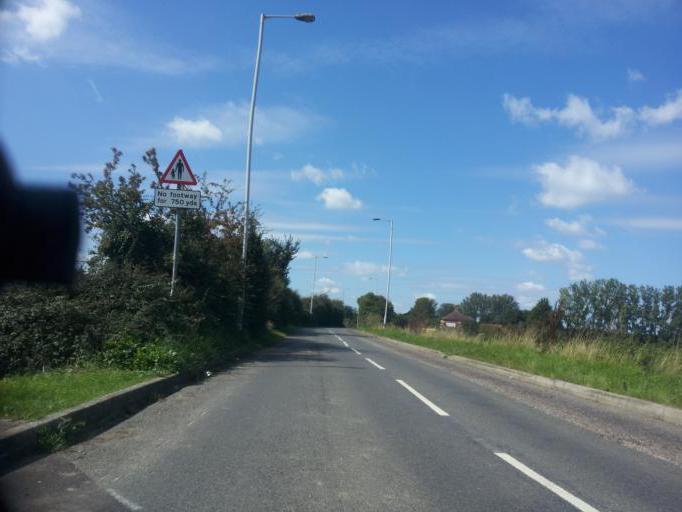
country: GB
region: England
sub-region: Kent
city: Sittingbourne
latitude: 51.3531
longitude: 0.7234
